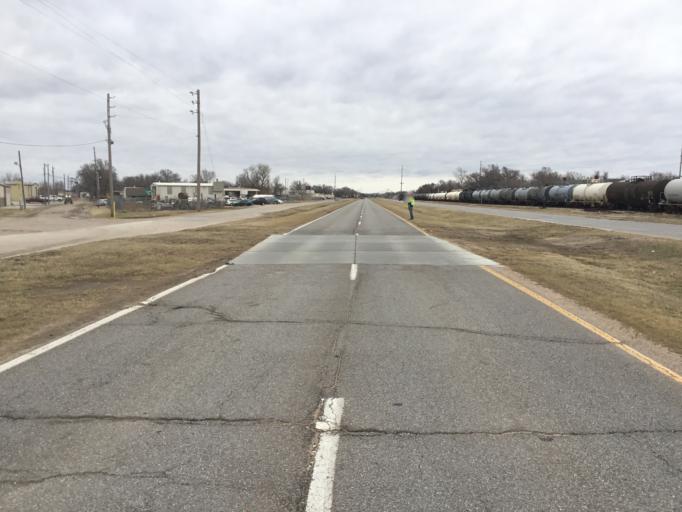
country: US
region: Kansas
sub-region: Sedgwick County
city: Wichita
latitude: 37.6592
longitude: -97.3823
